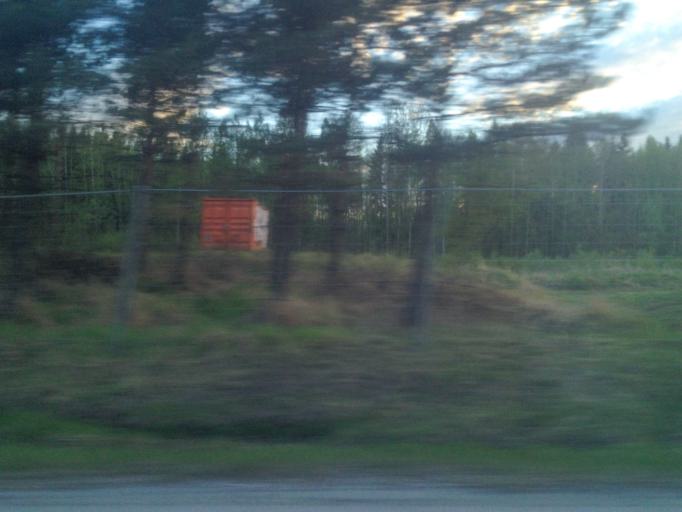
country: FI
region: Uusimaa
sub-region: Helsinki
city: Nurmijaervi
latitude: 60.5332
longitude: 24.8413
